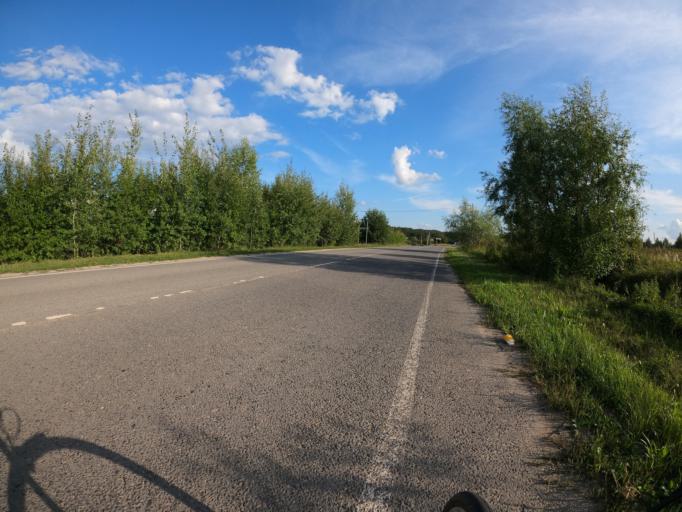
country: RU
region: Moskovskaya
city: Meshcherino
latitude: 55.1444
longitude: 38.4409
